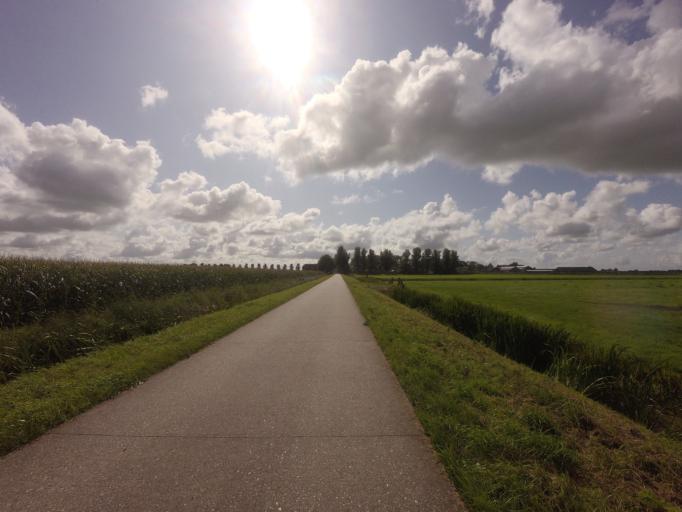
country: NL
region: Friesland
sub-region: Sudwest Fryslan
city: Sneek
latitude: 53.0612
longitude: 5.6314
